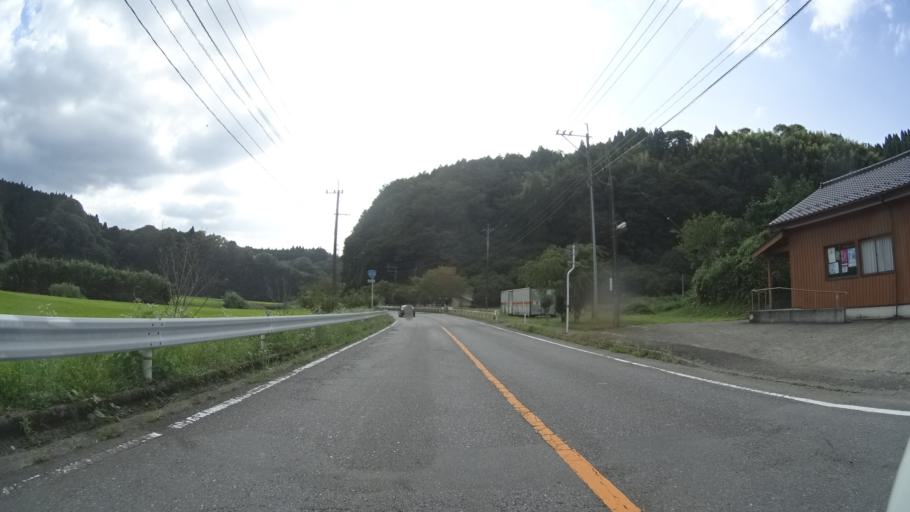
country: JP
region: Kumamoto
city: Aso
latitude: 32.6943
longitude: 131.1084
